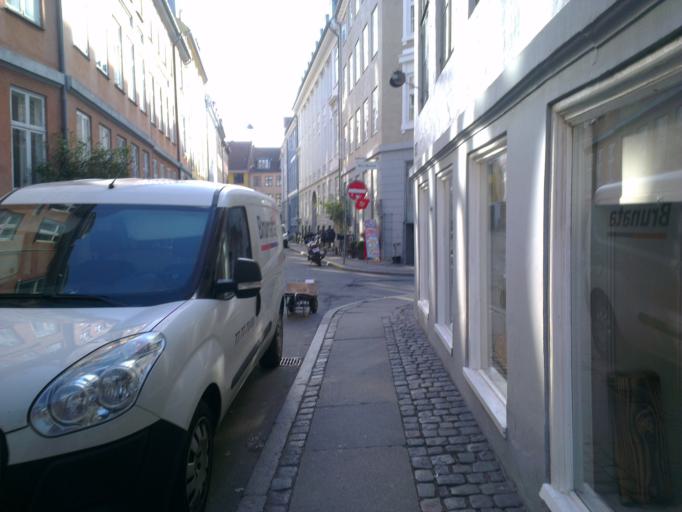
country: DK
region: Capital Region
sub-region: Kobenhavn
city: Copenhagen
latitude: 55.6782
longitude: 12.5750
